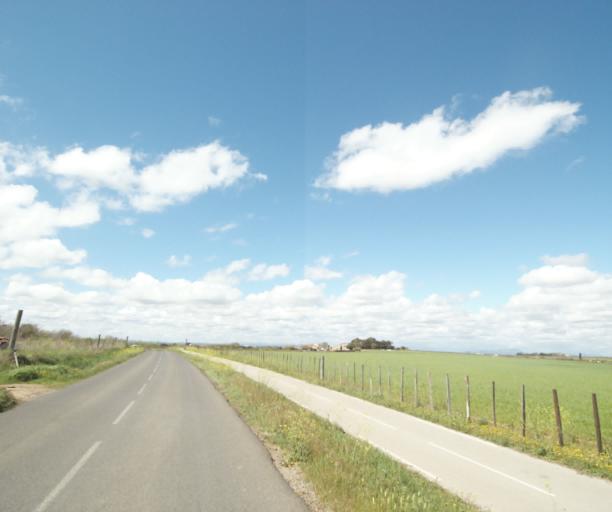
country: FR
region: Languedoc-Roussillon
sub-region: Departement de l'Herault
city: Lattes
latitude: 43.5595
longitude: 3.9277
